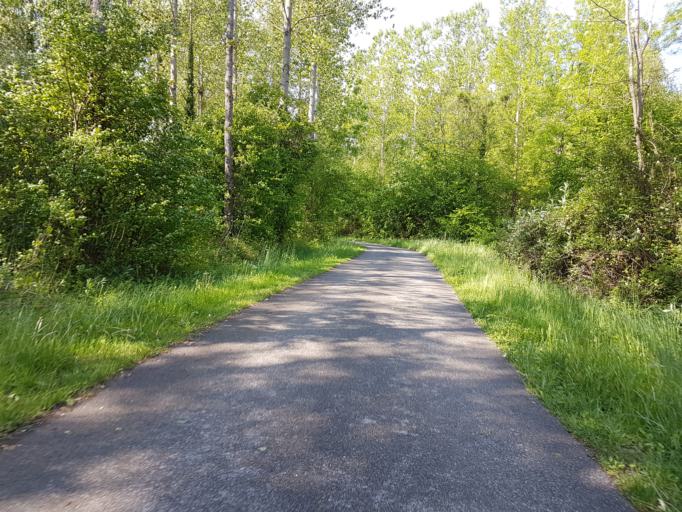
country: FR
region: Rhone-Alpes
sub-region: Departement de l'Ain
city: Culoz
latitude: 45.8735
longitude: 5.8221
